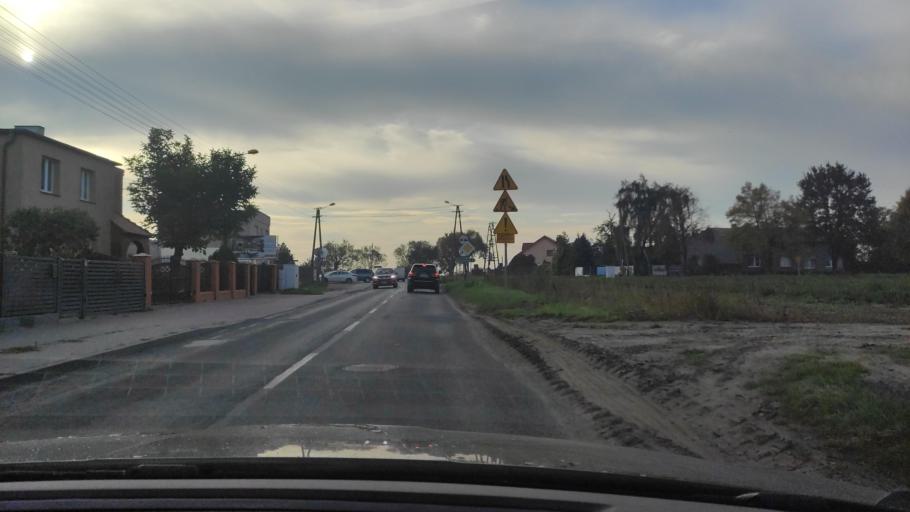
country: PL
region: Greater Poland Voivodeship
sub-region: Powiat poznanski
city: Kleszczewo
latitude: 52.3791
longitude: 17.1655
